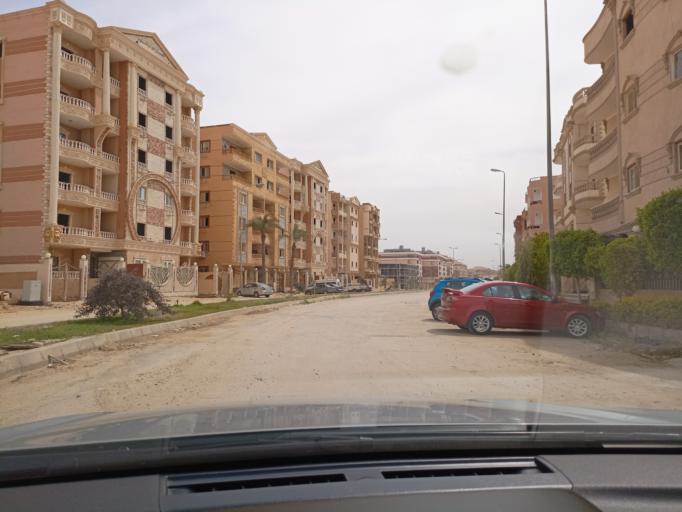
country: EG
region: Muhafazat al Qalyubiyah
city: Al Khankah
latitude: 30.2503
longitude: 31.5028
